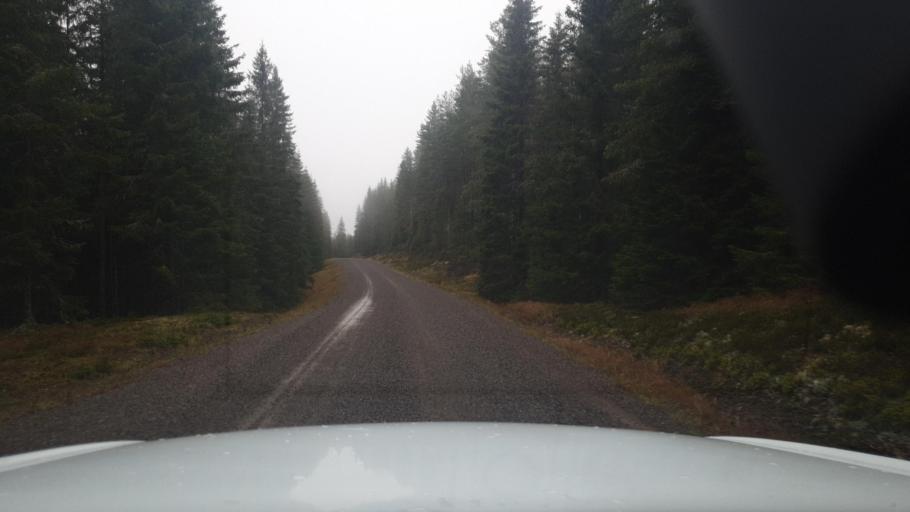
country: SE
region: Vaermland
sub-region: Eda Kommun
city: Charlottenberg
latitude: 60.0925
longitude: 12.6147
